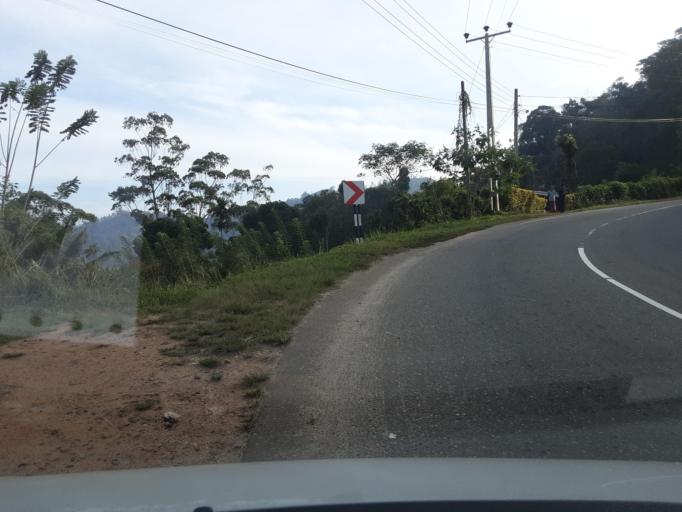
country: LK
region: Uva
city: Badulla
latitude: 6.9295
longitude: 80.9650
